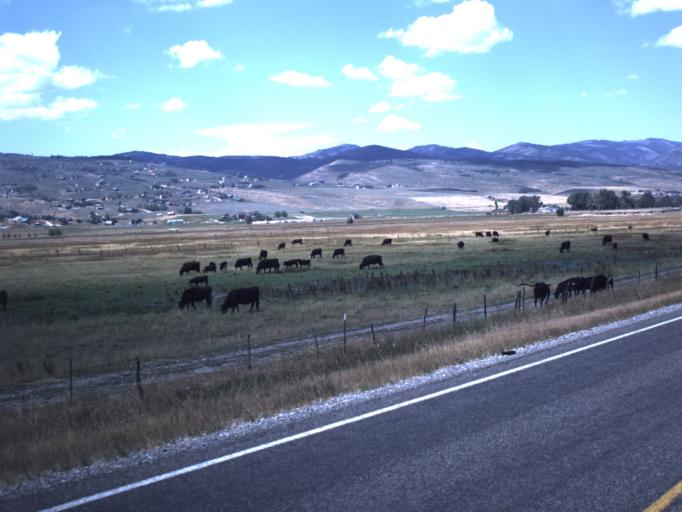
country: US
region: Utah
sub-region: Rich County
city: Randolph
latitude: 41.9016
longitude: -111.3732
